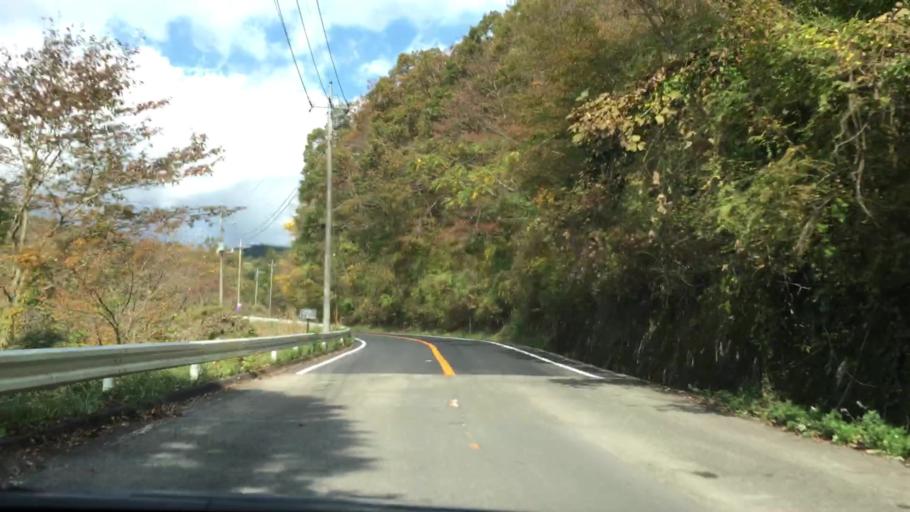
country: JP
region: Shizuoka
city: Gotemba
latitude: 35.3776
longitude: 138.9441
